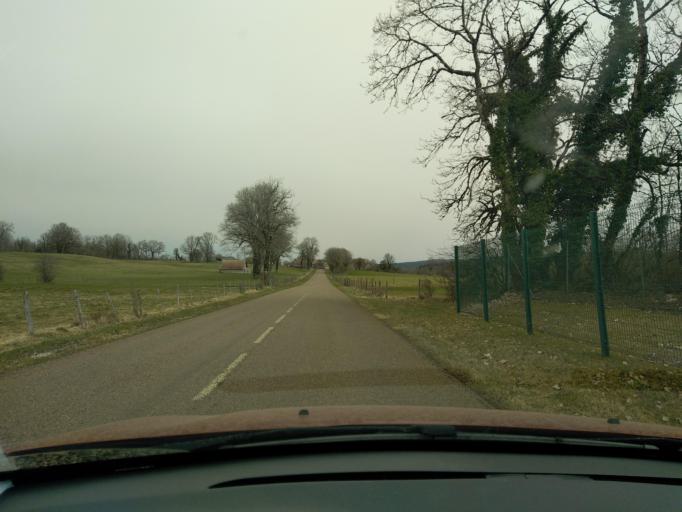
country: FR
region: Franche-Comte
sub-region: Departement du Jura
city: Champagnole
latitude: 46.7702
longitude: 5.8800
